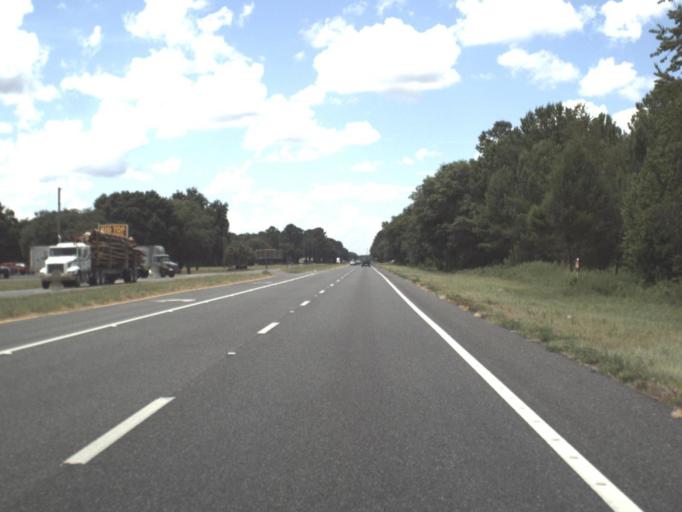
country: US
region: Florida
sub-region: Taylor County
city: Perry
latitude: 30.1604
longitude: -83.6223
